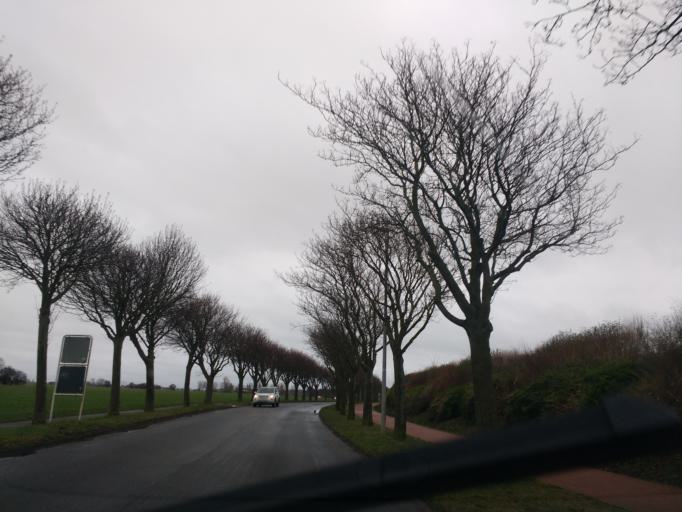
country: DE
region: Schleswig-Holstein
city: Burg auf Fehmarn
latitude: 54.4294
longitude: 11.2015
